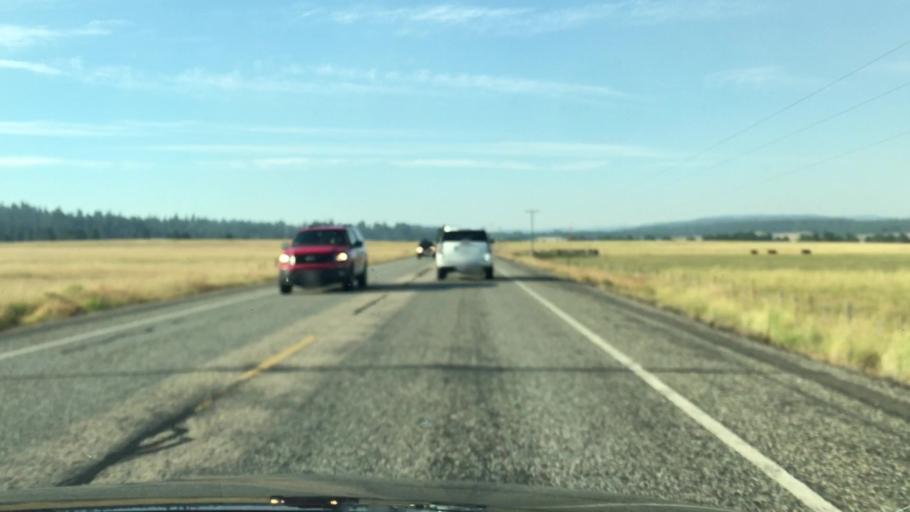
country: US
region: Idaho
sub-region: Valley County
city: Cascade
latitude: 44.3463
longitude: -116.0269
